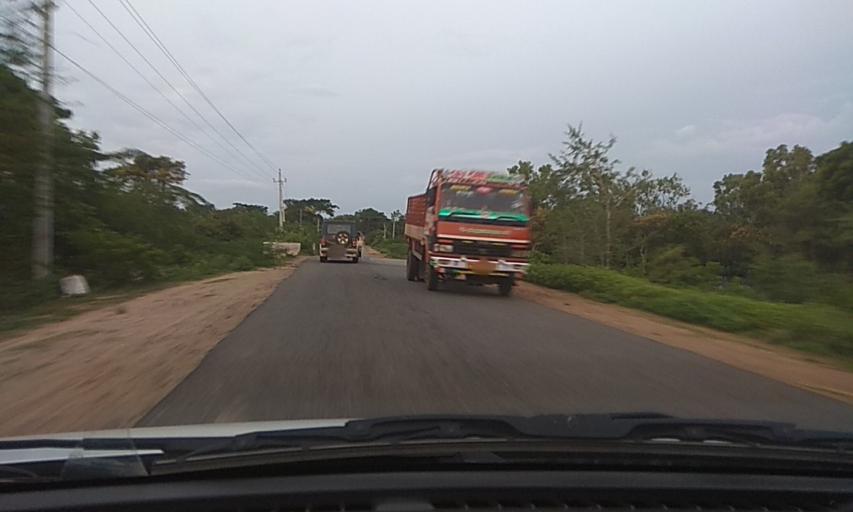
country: IN
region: Karnataka
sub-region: Chamrajnagar
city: Gundlupet
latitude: 11.8143
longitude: 76.7629
